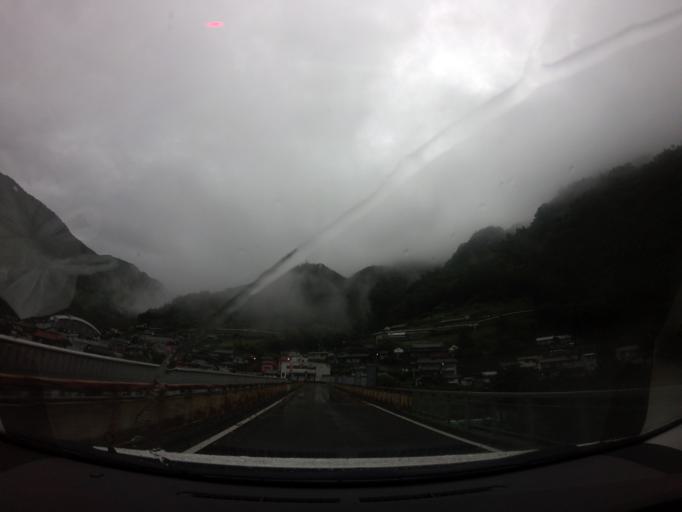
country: JP
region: Wakayama
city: Shingu
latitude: 33.9477
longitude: 135.8045
